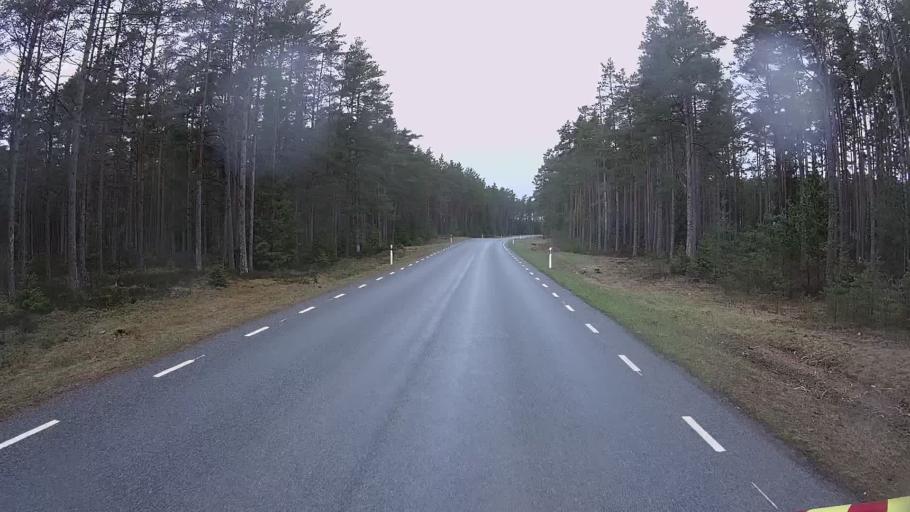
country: EE
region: Hiiumaa
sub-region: Kaerdla linn
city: Kardla
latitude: 58.9101
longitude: 22.3909
